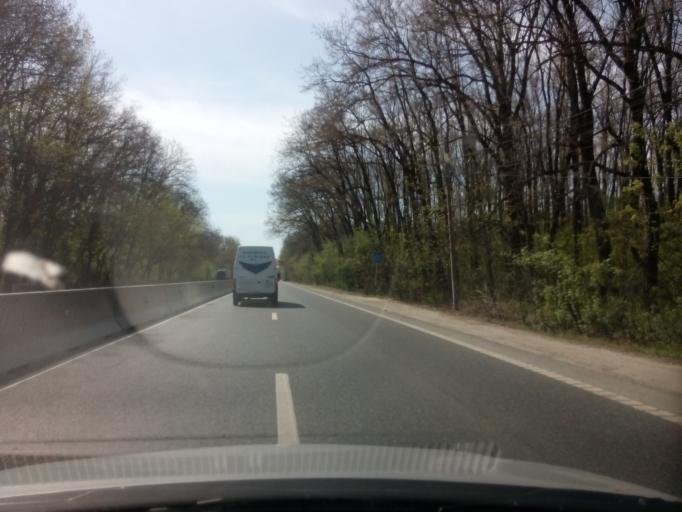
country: RO
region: Ilfov
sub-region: Comuna Corbeanca
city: Corbeanca
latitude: 44.5887
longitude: 26.0707
